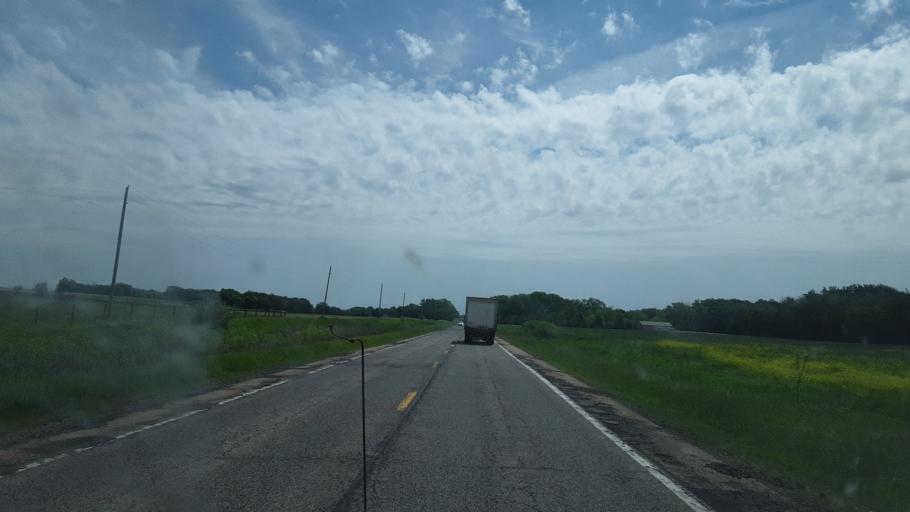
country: US
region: Illinois
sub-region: Logan County
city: Atlanta
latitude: 40.3104
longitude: -89.2956
